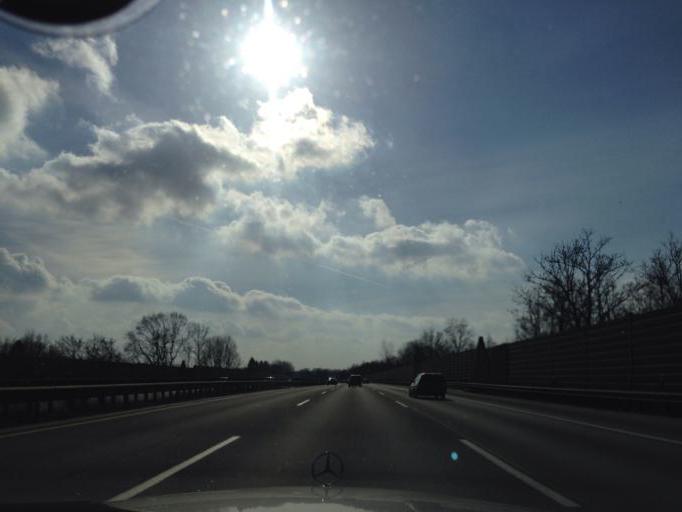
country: DE
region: Hamburg
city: Harburg
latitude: 53.4213
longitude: 10.0323
